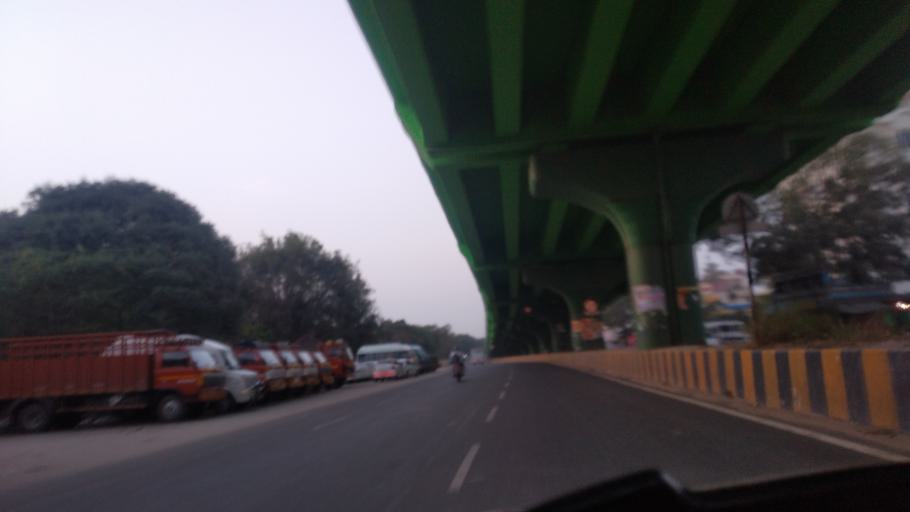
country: IN
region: Tamil Nadu
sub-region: Coimbatore
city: Coimbatore
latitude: 11.0134
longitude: 76.9678
